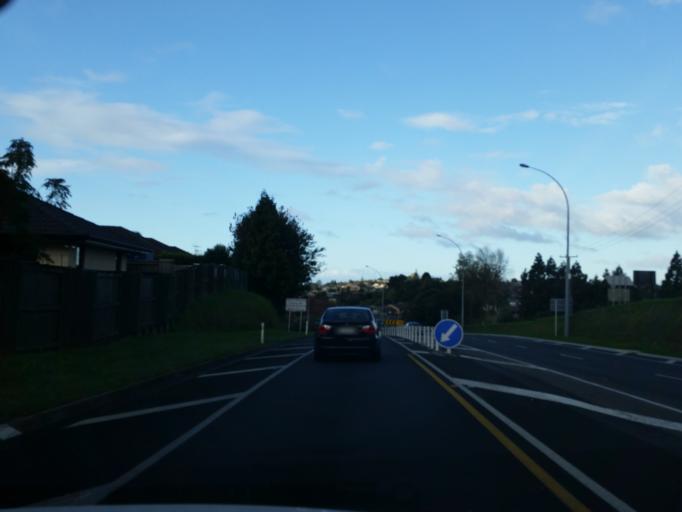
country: NZ
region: Bay of Plenty
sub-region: Tauranga City
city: Tauranga
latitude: -37.6953
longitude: 176.1161
